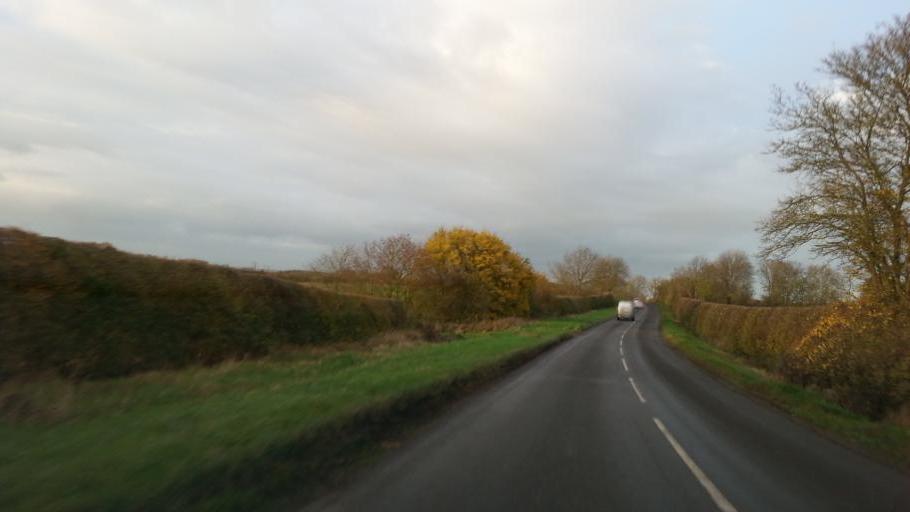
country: GB
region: England
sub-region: Lincolnshire
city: Long Bennington
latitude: 53.0086
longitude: -0.8044
